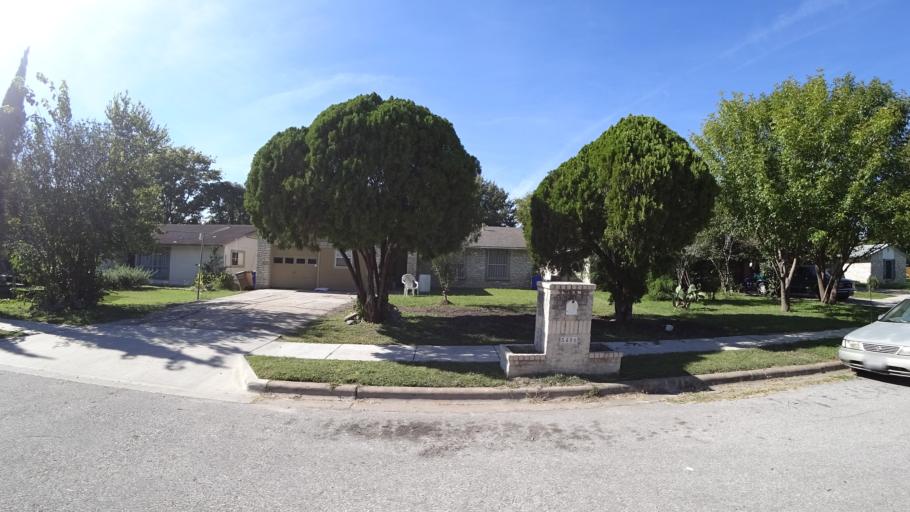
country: US
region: Texas
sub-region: Travis County
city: Onion Creek
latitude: 30.1961
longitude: -97.7504
